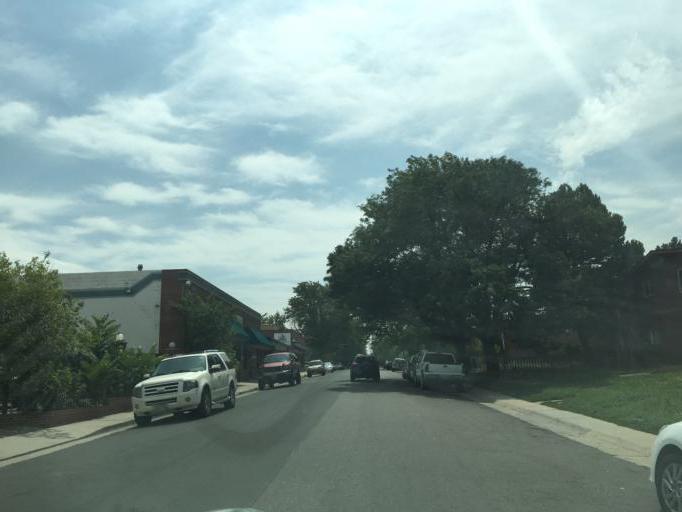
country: US
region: Colorado
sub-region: Adams County
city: Aurora
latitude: 39.7396
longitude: -104.8588
